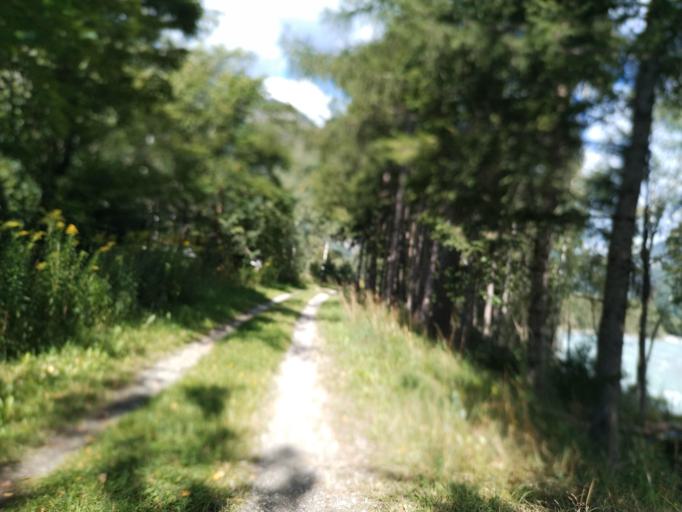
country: AT
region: Tyrol
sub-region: Politischer Bezirk Lienz
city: Schlaiten
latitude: 46.9047
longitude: 12.6247
